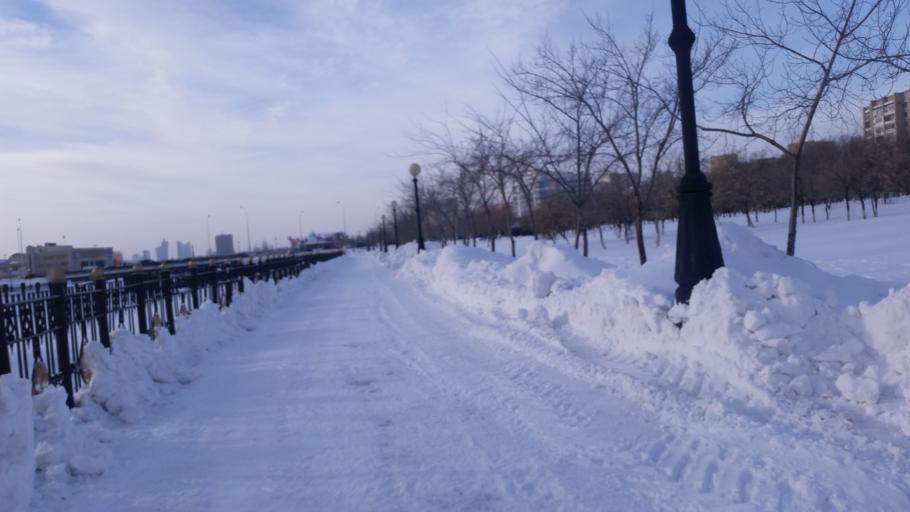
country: KZ
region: Astana Qalasy
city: Astana
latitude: 51.1618
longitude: 71.4716
